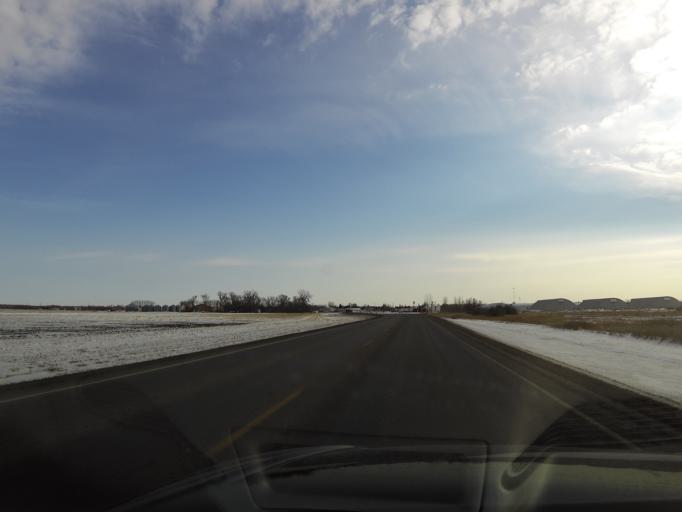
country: US
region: North Dakota
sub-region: Walsh County
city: Grafton
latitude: 48.5767
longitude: -97.1787
